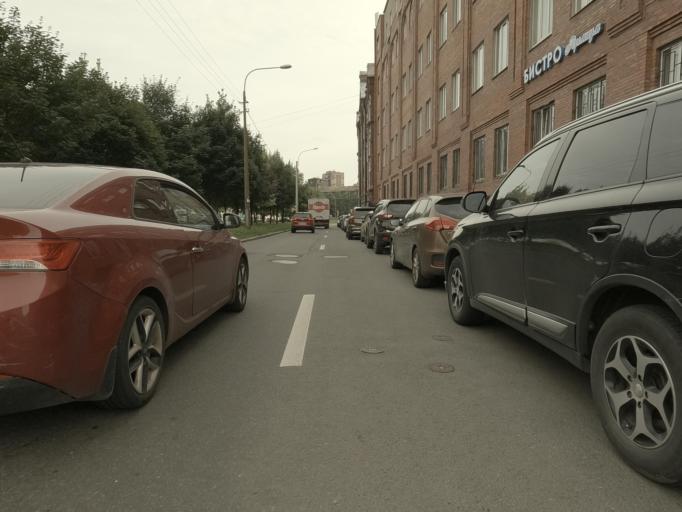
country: RU
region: St.-Petersburg
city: Admiralteisky
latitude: 59.9111
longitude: 30.2869
